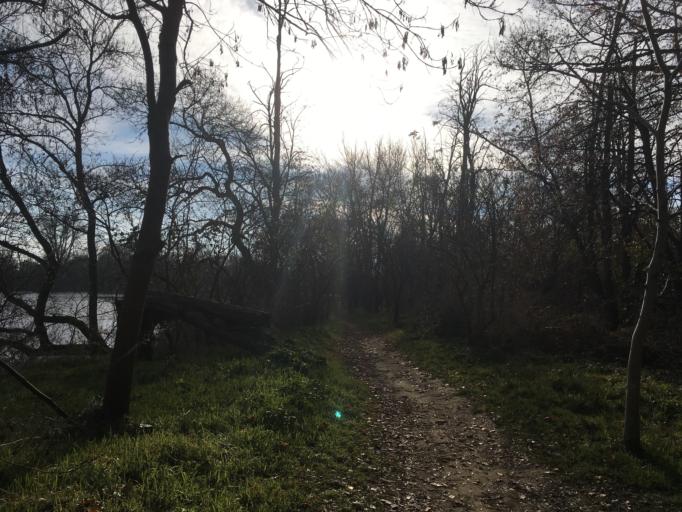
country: FR
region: Midi-Pyrenees
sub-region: Departement de la Haute-Garonne
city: Blagnac
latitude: 43.6532
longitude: 1.4042
